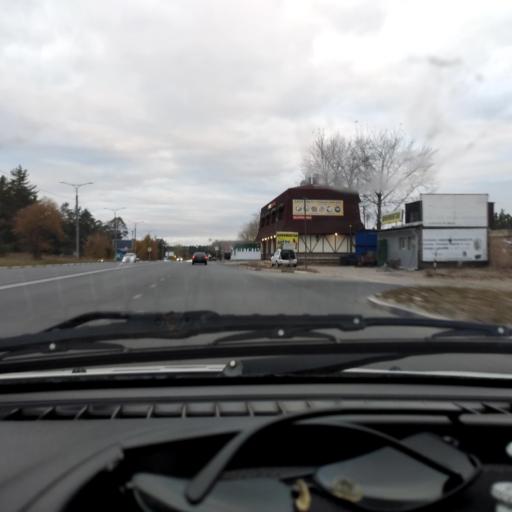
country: RU
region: Samara
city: Zhigulevsk
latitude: 53.4935
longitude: 49.4741
